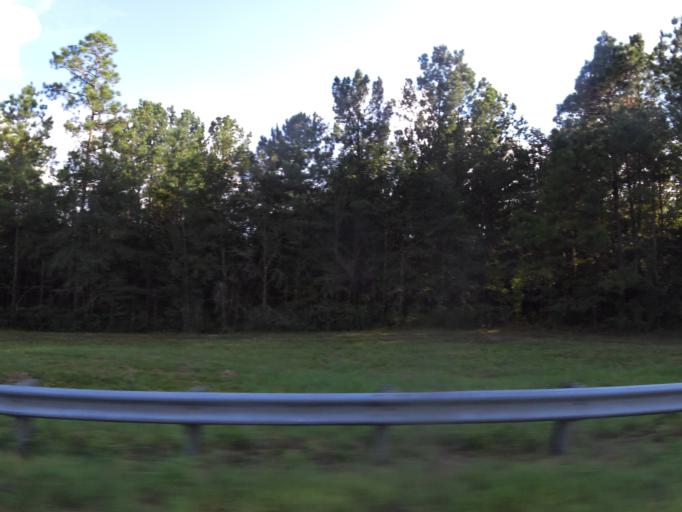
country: US
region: Georgia
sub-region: Lowndes County
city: Remerton
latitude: 30.8001
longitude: -83.3839
